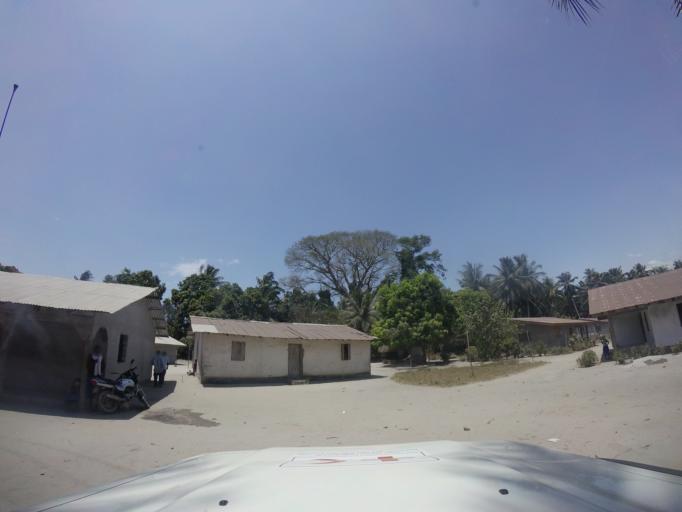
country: LR
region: Grand Cape Mount
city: Robertsport
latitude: 6.9122
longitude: -11.4197
